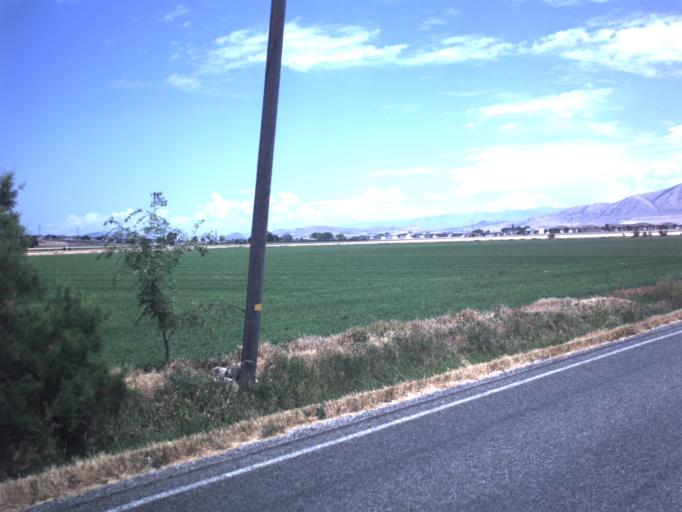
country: US
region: Utah
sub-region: Box Elder County
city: Tremonton
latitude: 41.7105
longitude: -112.2192
